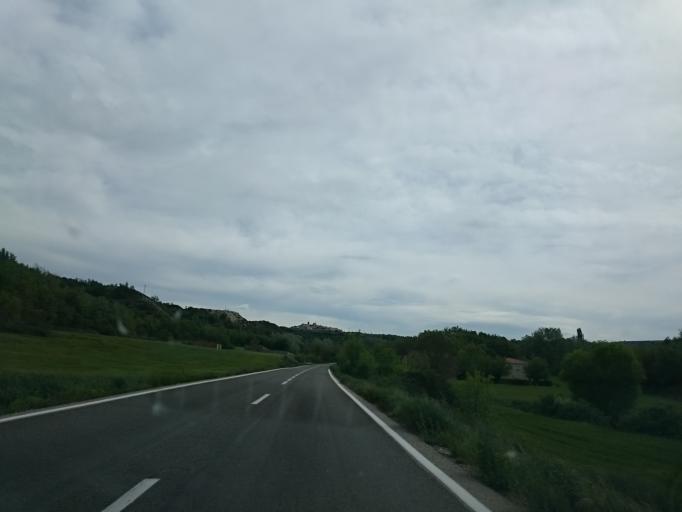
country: ES
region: Catalonia
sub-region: Provincia de Lleida
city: Ivorra
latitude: 41.7847
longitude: 1.3931
